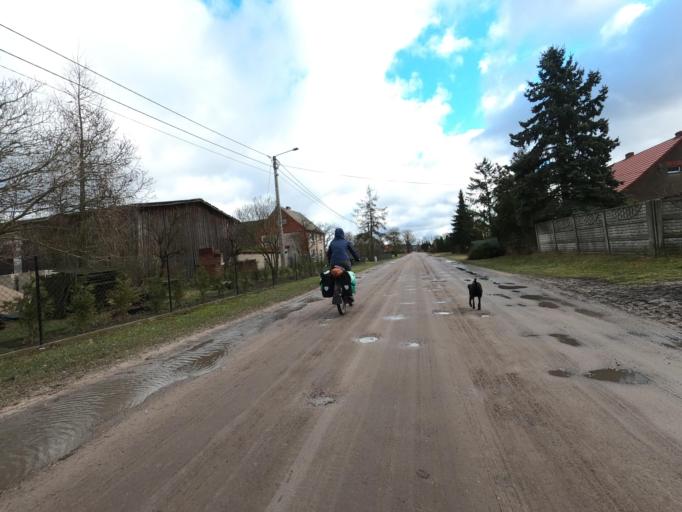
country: PL
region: Greater Poland Voivodeship
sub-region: Powiat pilski
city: Miasteczko Krajenskie
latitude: 53.1127
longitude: 17.0010
